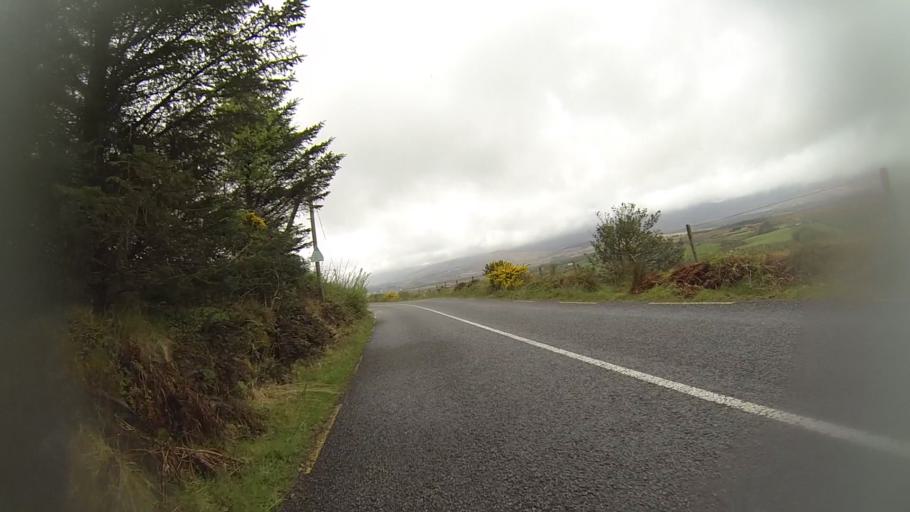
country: IE
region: Munster
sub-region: Ciarrai
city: Killorglin
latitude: 51.8543
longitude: -9.8744
